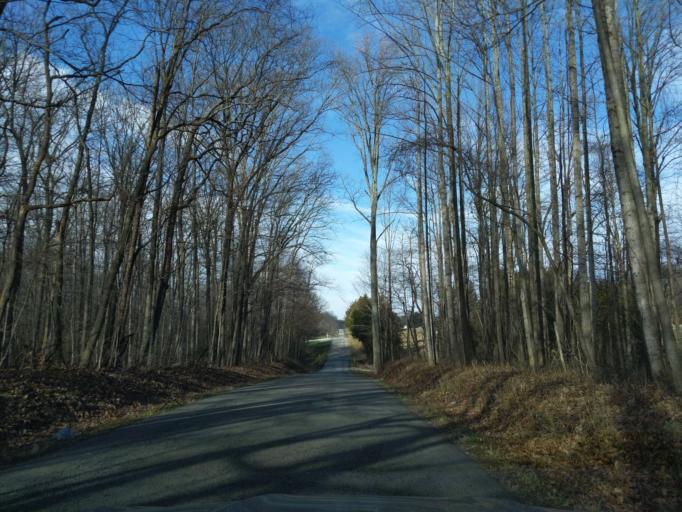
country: US
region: Indiana
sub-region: Decatur County
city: Greensburg
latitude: 39.2809
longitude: -85.4236
